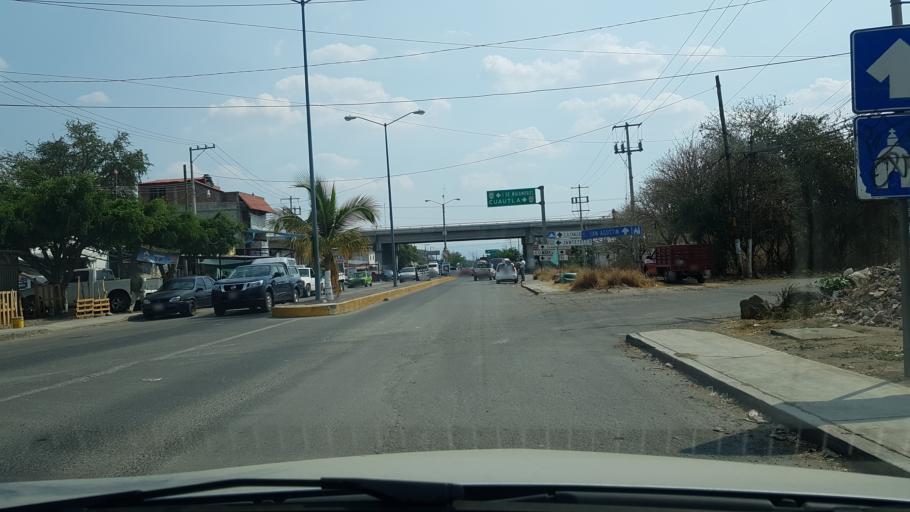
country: MX
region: Morelos
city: Amayuca
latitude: 18.7189
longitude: -98.7946
